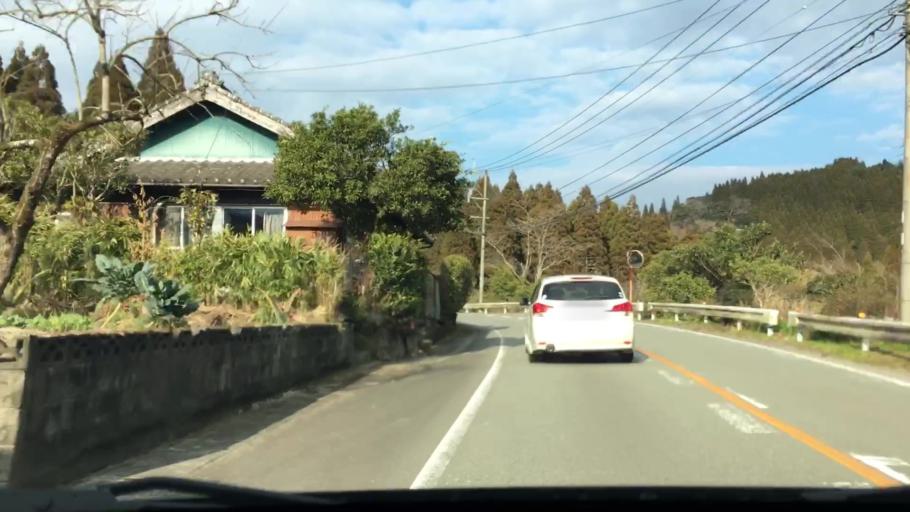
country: JP
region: Miyazaki
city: Nichinan
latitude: 31.7251
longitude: 131.3304
